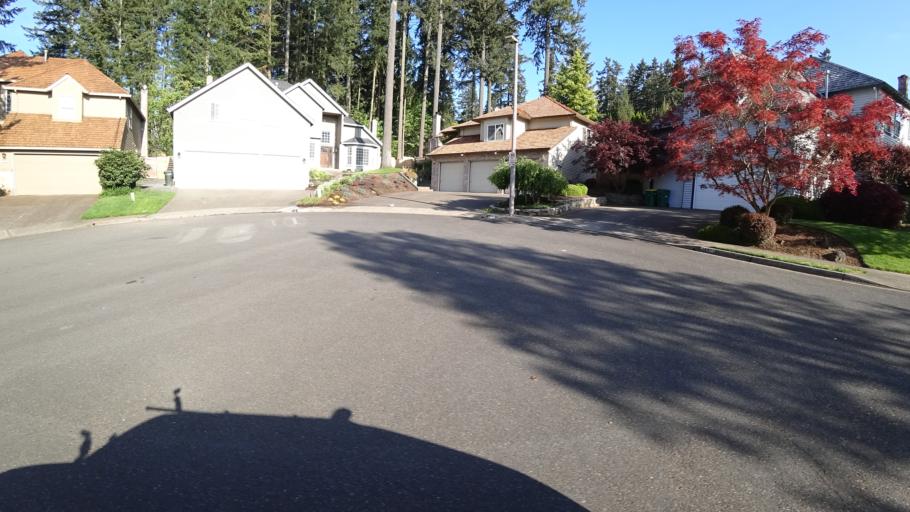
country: US
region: Oregon
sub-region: Washington County
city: King City
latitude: 45.4444
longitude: -122.8365
